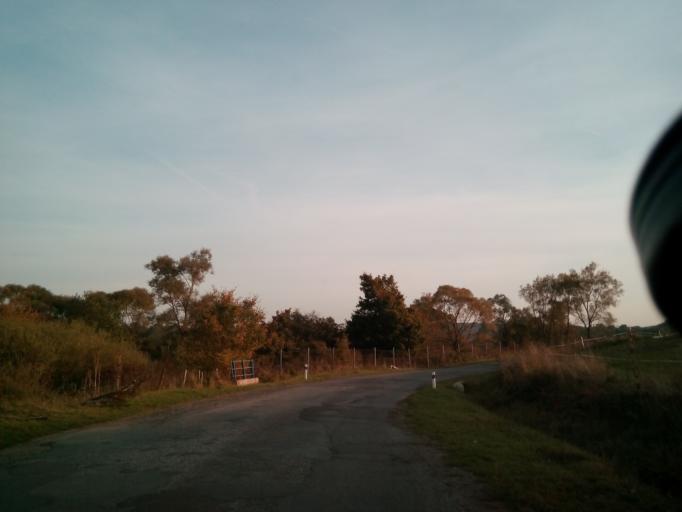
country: SK
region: Presovsky
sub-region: Okres Bardejov
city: Bardejov
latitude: 49.3482
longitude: 21.3940
